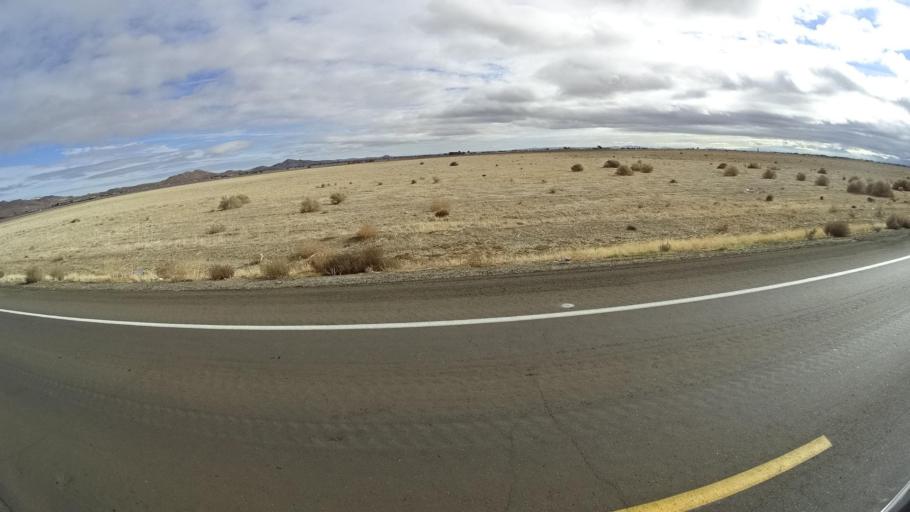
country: US
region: California
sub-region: Kern County
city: Rosamond
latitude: 34.8470
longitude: -118.2908
